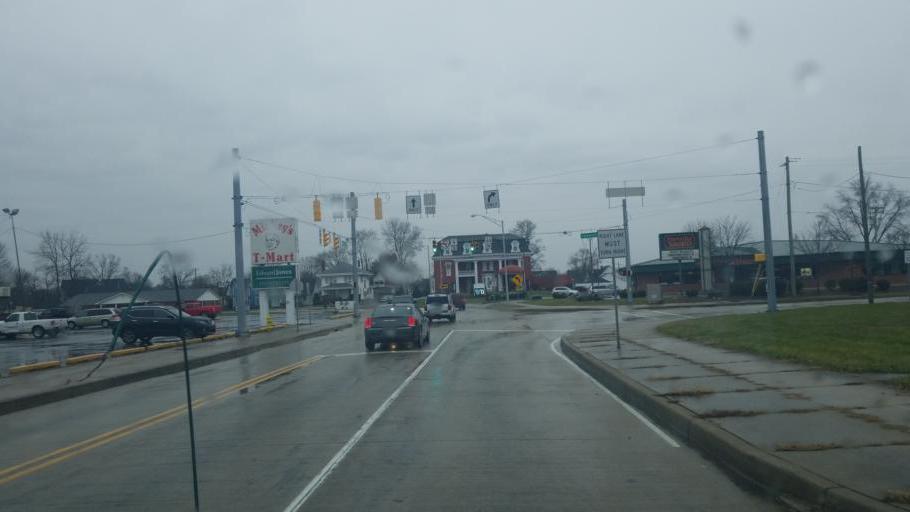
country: US
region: Indiana
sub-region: Shelby County
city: Shelbyville
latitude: 39.5182
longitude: -85.7771
